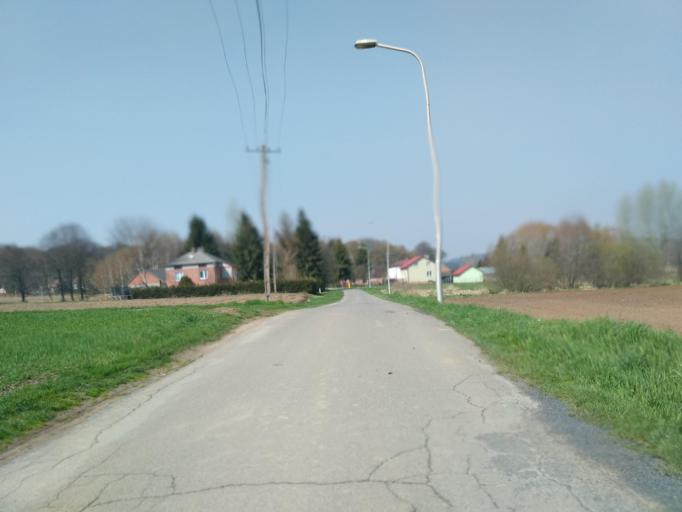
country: PL
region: Subcarpathian Voivodeship
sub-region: Powiat brzozowski
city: Turze Pole
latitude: 49.6451
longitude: 22.0100
